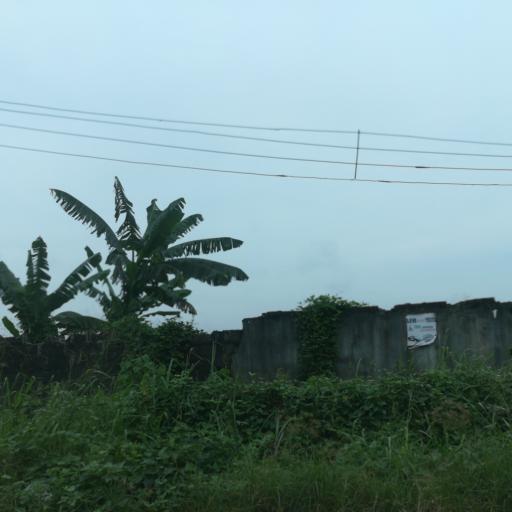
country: NG
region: Rivers
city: Port Harcourt
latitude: 4.8230
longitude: 7.0625
